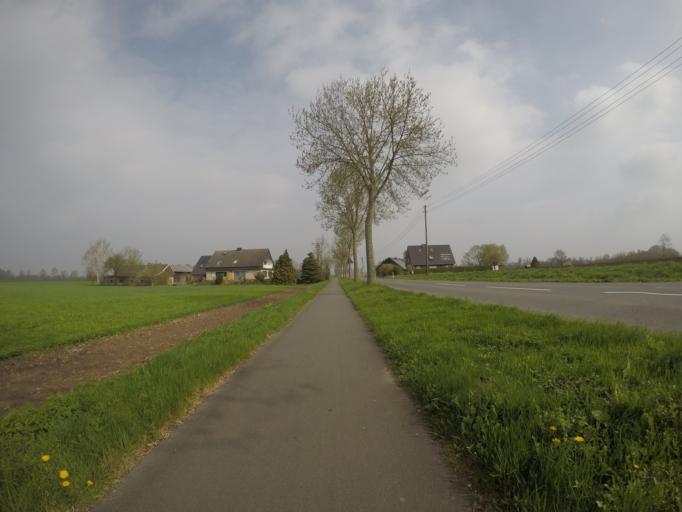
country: DE
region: North Rhine-Westphalia
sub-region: Regierungsbezirk Munster
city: Isselburg
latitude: 51.8434
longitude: 6.5016
